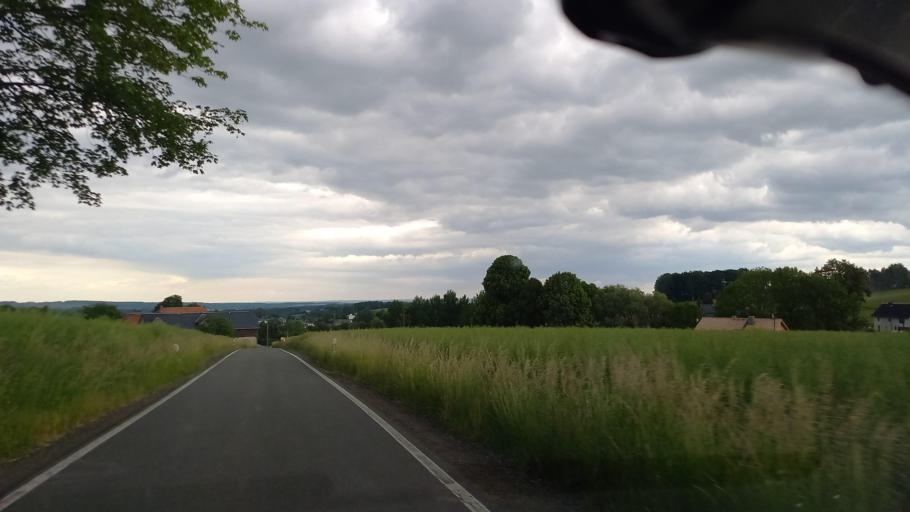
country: DE
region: Saxony
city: Rodewisch
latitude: 50.5703
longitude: 12.4433
